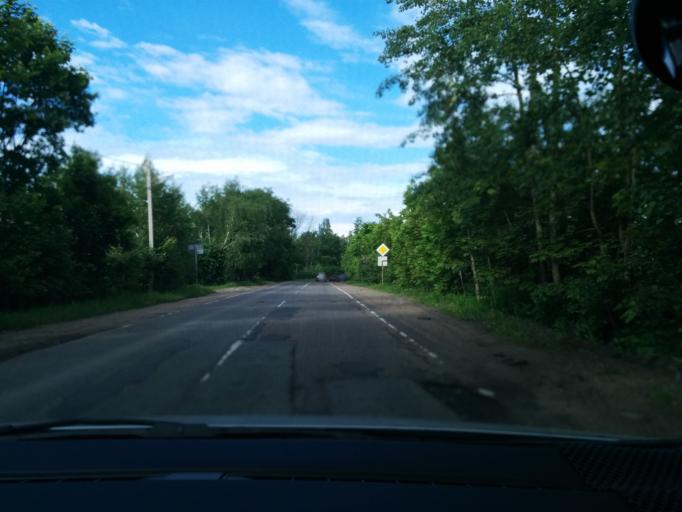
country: RU
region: Moskovskaya
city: Lugovaya
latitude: 56.0511
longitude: 37.4820
